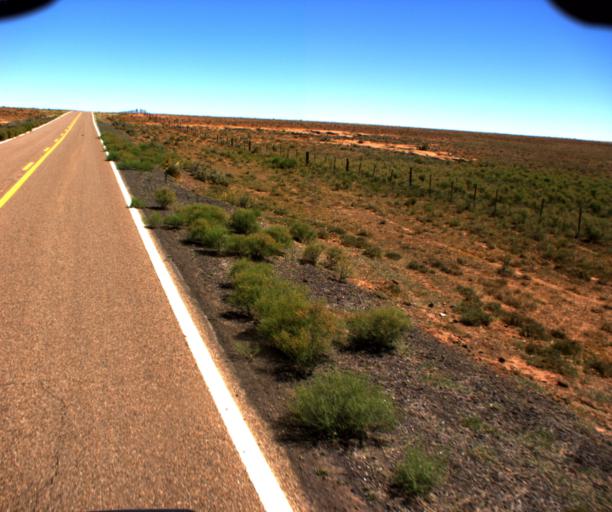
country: US
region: Arizona
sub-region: Navajo County
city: Winslow
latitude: 34.8470
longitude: -110.6677
